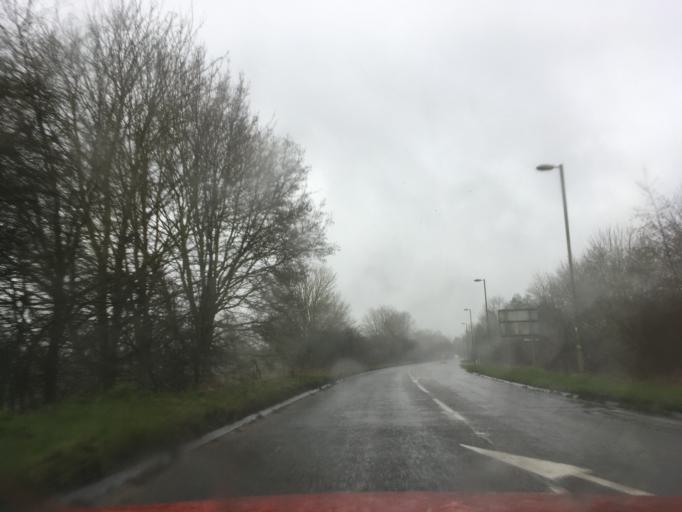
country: GB
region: England
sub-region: Oxfordshire
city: Eynsham
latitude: 51.7825
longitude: -1.3655
